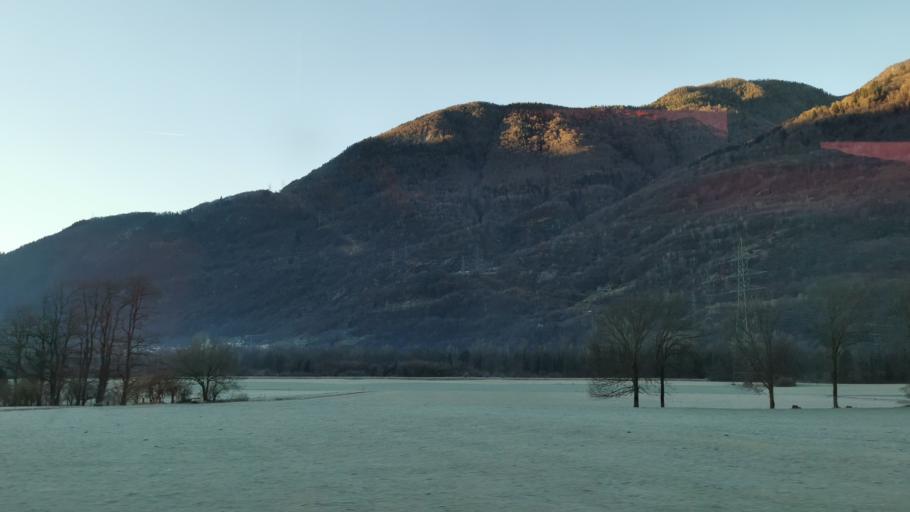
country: CH
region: Ticino
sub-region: Riviera District
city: Claro
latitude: 46.2453
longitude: 9.0241
